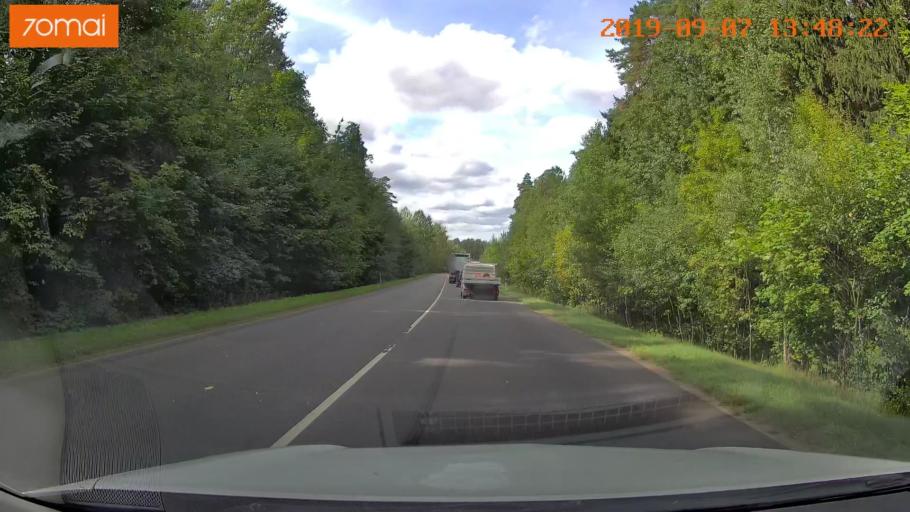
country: LT
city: Baltoji Voke
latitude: 54.6019
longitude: 25.2036
